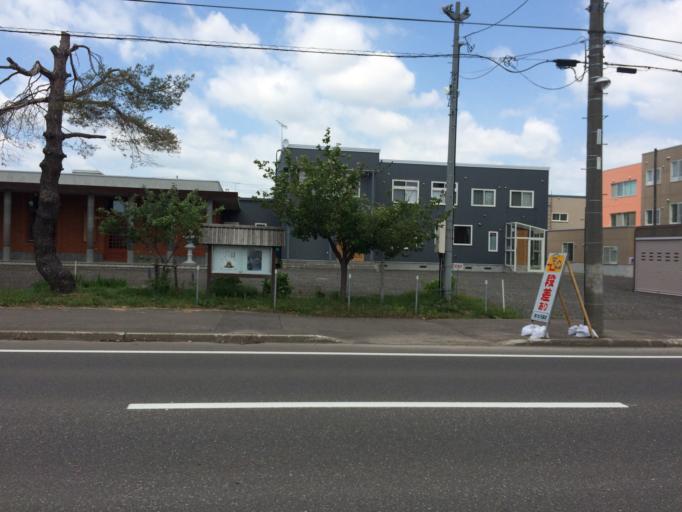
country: JP
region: Hokkaido
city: Niseko Town
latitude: 42.8989
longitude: 140.7513
